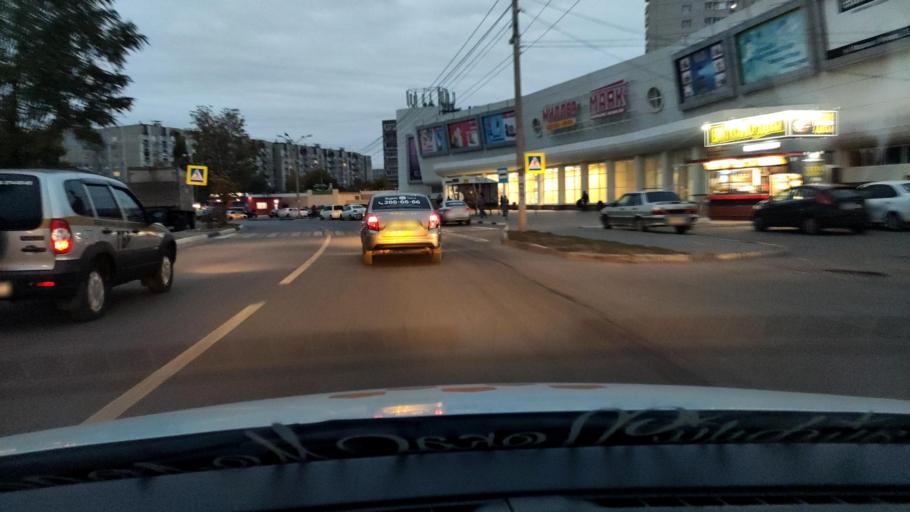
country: RU
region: Voronezj
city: Podgornoye
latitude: 51.7163
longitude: 39.1711
